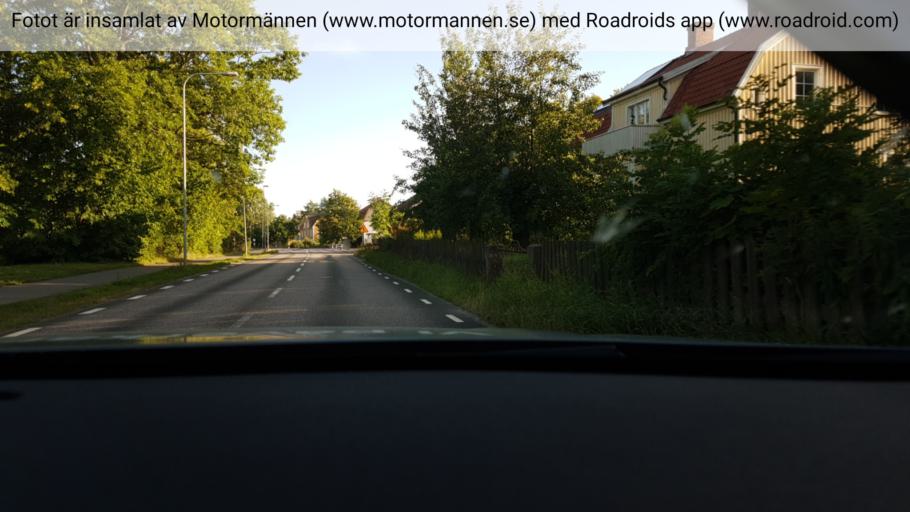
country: SE
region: Vaestra Goetaland
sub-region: Toreboda Kommun
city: Toereboda
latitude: 58.5782
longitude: 14.0046
